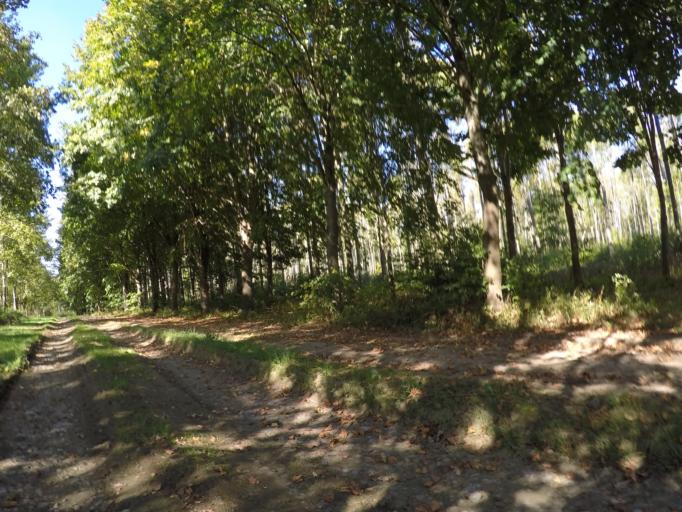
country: BE
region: Wallonia
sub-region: Province de Namur
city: Assesse
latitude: 50.3139
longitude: 5.0128
